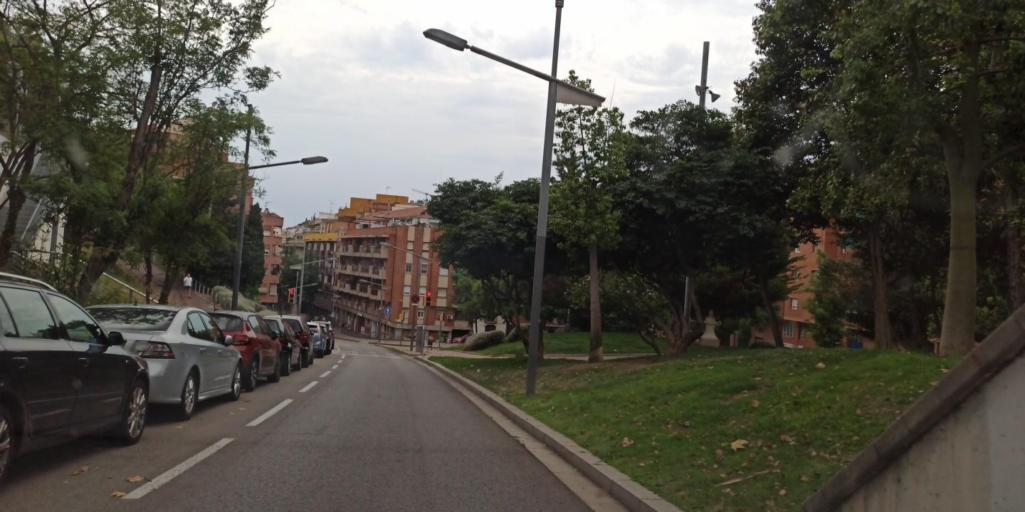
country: ES
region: Catalonia
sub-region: Provincia de Barcelona
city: Horta-Guinardo
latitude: 41.4311
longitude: 2.1638
